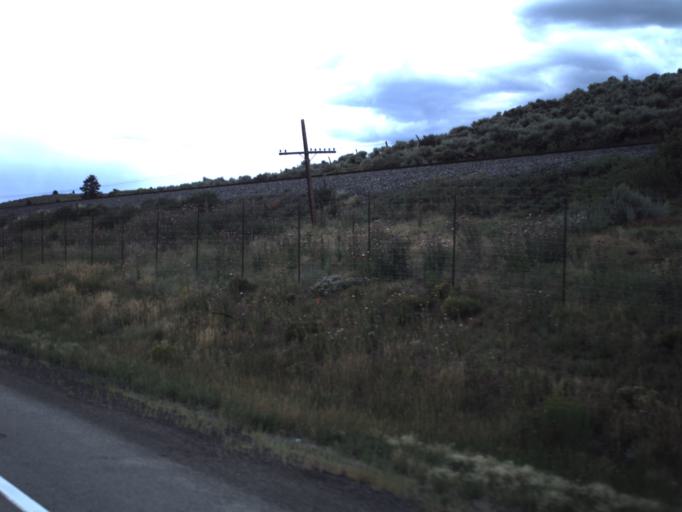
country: US
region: Utah
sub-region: Carbon County
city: Helper
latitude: 39.8955
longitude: -111.0537
